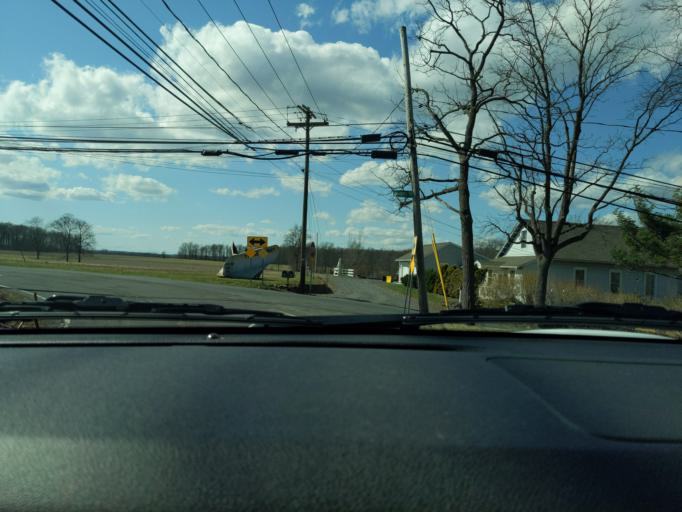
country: US
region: Pennsylvania
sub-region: Bucks County
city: Richlandtown
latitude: 40.4601
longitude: -75.2915
